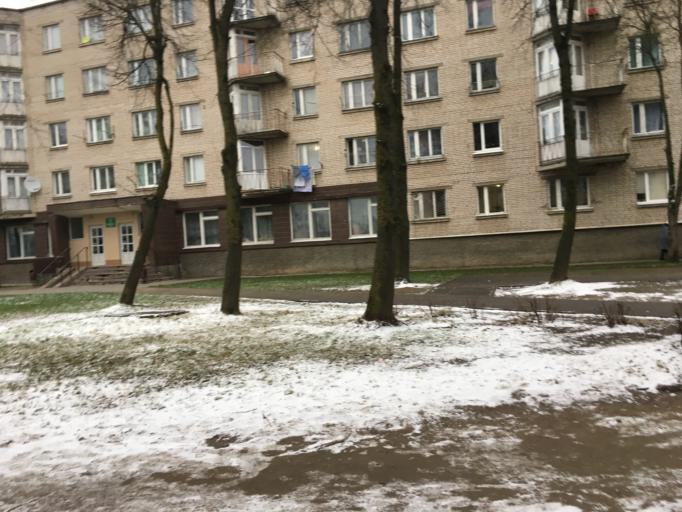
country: BY
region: Grodnenskaya
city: Hrodna
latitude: 53.7002
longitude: 23.8145
